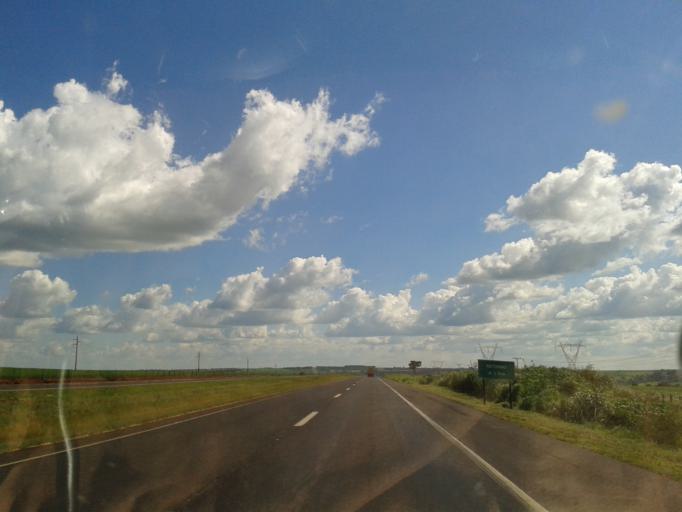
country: BR
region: Goias
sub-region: Goiatuba
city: Goiatuba
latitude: -17.9773
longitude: -49.2561
